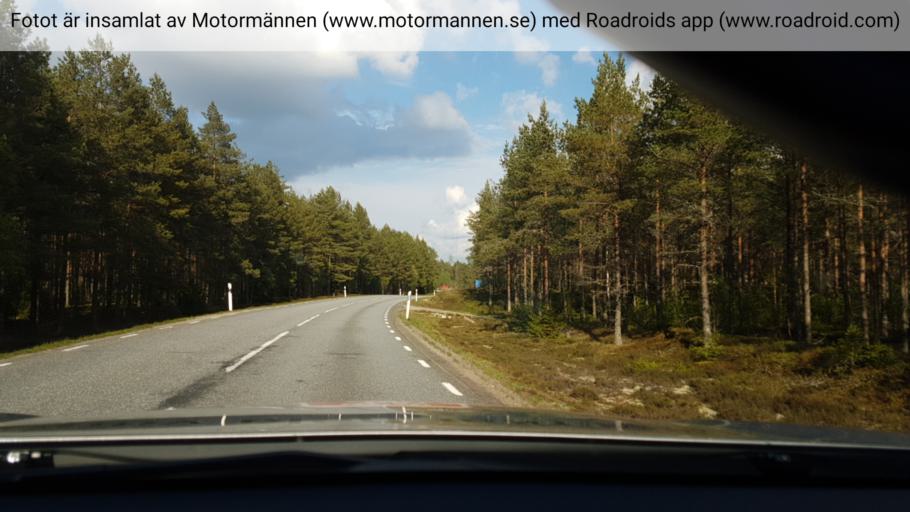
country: SE
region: Joenkoeping
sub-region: Vaggeryds Kommun
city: Skillingaryd
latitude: 57.3834
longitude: 13.9843
